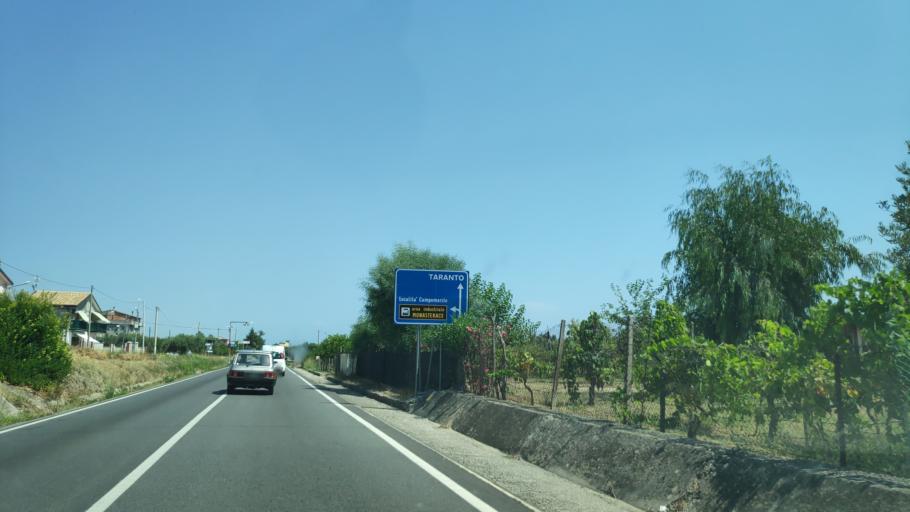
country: IT
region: Calabria
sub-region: Provincia di Catanzaro
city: Guardavalle Marina
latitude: 38.4615
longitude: 16.5796
